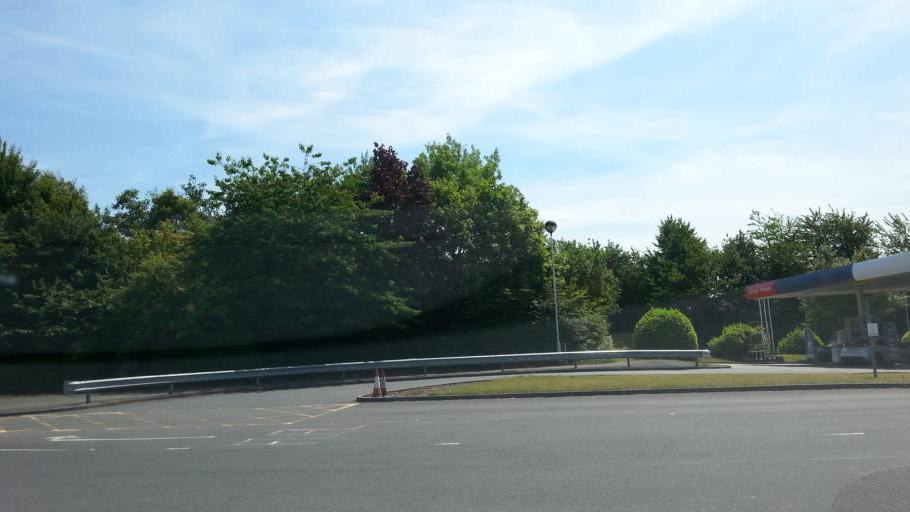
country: GB
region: England
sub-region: Staffordshire
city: Great Wyrley
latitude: 52.6914
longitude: -1.9988
